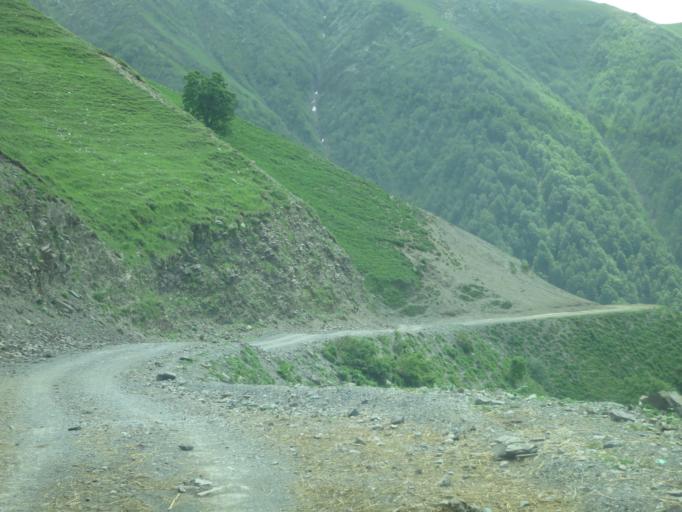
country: GE
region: Kakheti
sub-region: Telavi
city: Telavi
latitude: 42.2531
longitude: 45.4999
